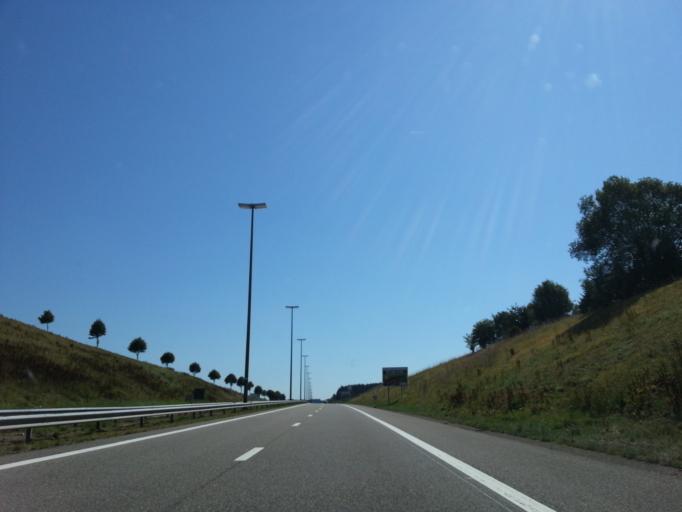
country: BE
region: Wallonia
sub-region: Province de Liege
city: Saint-Vith
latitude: 50.2624
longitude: 6.1265
